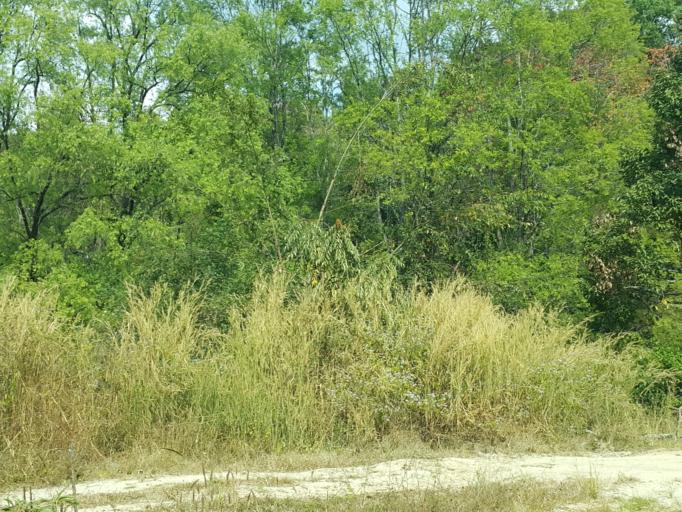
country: TH
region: Chiang Mai
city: Om Koi
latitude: 17.8014
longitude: 98.3667
